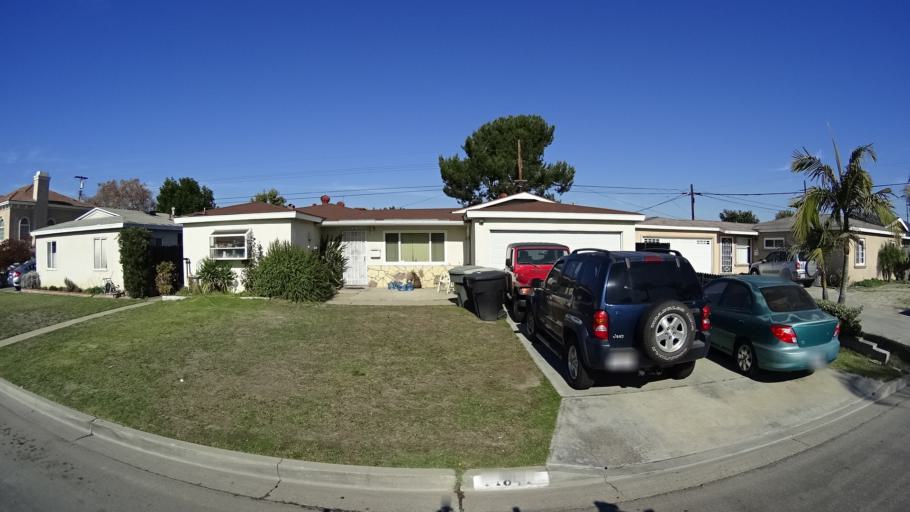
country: US
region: California
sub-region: Orange County
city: Garden Grove
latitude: 33.7848
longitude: -117.9261
